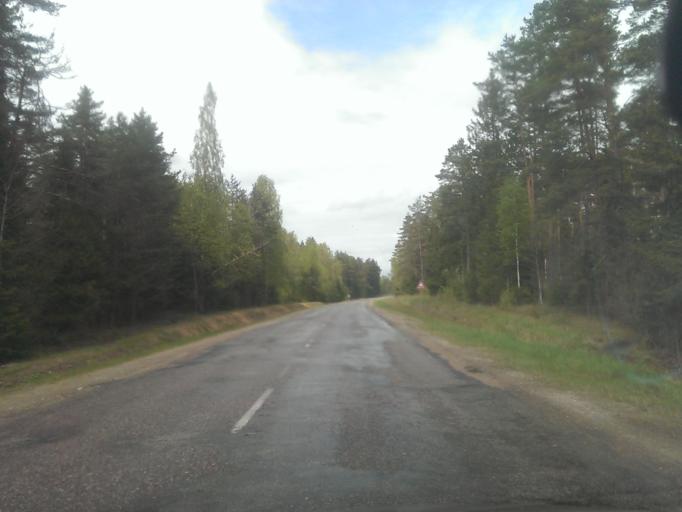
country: LV
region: Ventspils Rajons
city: Piltene
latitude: 57.0925
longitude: 21.7781
